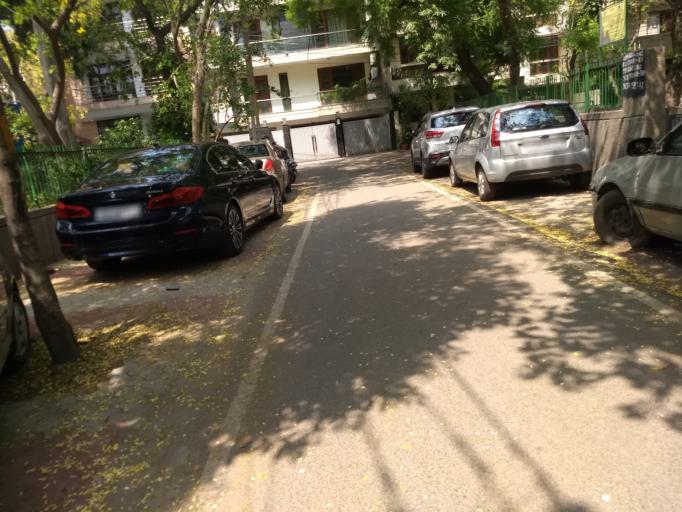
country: IN
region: NCT
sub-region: New Delhi
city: New Delhi
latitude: 28.5572
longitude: 77.2146
